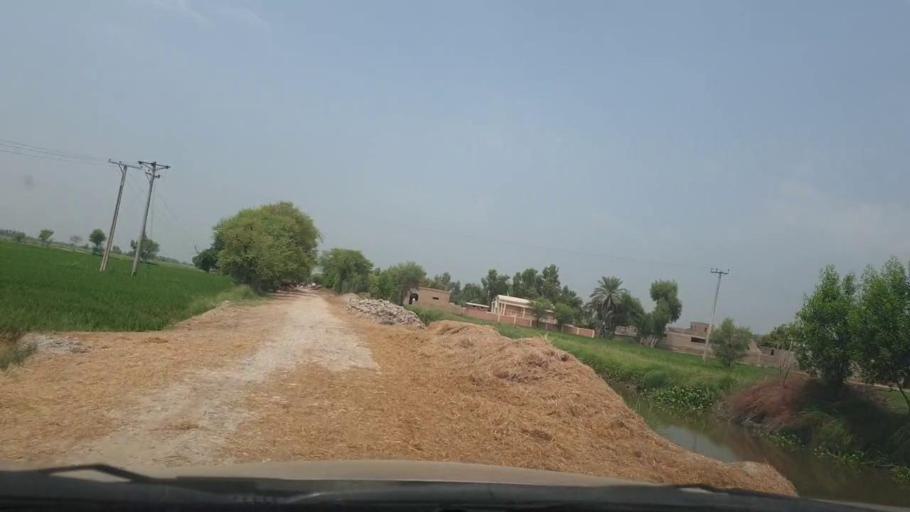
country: PK
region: Sindh
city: Naudero
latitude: 27.6882
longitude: 68.2465
